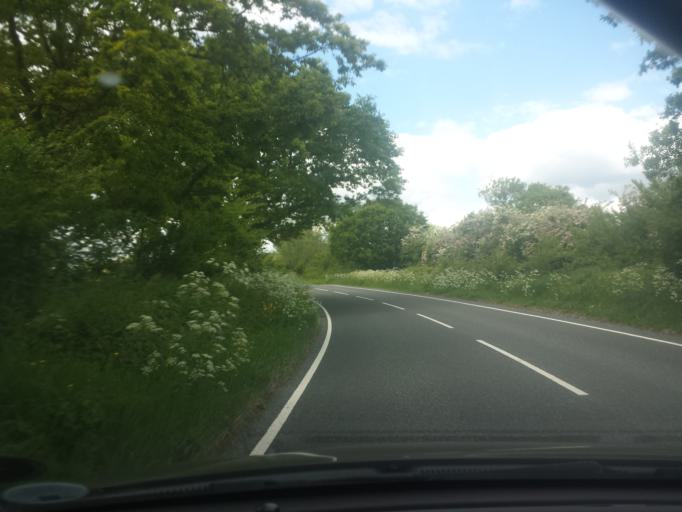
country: GB
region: England
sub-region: Essex
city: Little Clacton
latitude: 51.8302
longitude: 1.1583
